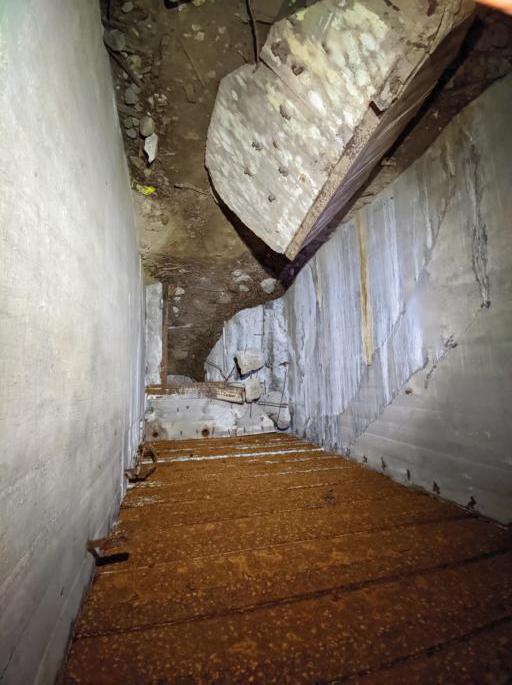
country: PL
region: Lubusz
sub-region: Powiat miedzyrzecki
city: Bledzew
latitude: 52.4294
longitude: 15.4730
